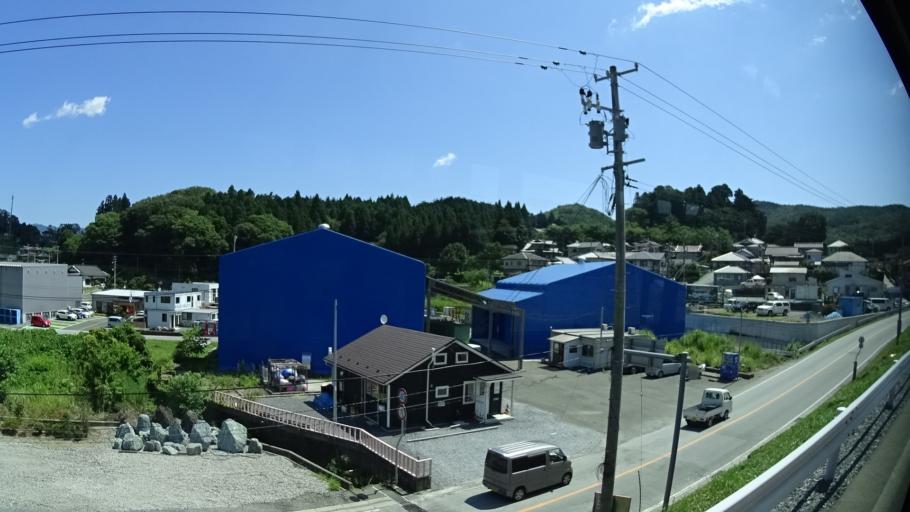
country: JP
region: Iwate
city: Ofunato
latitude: 39.0142
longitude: 141.7150
